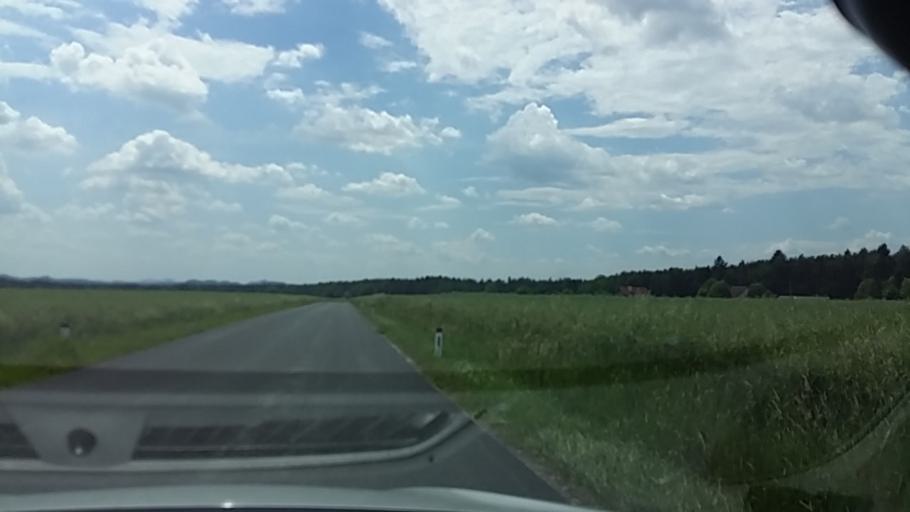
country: AT
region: Styria
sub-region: Politischer Bezirk Hartberg-Fuerstenfeld
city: Bad Blumau
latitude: 47.1157
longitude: 15.9987
